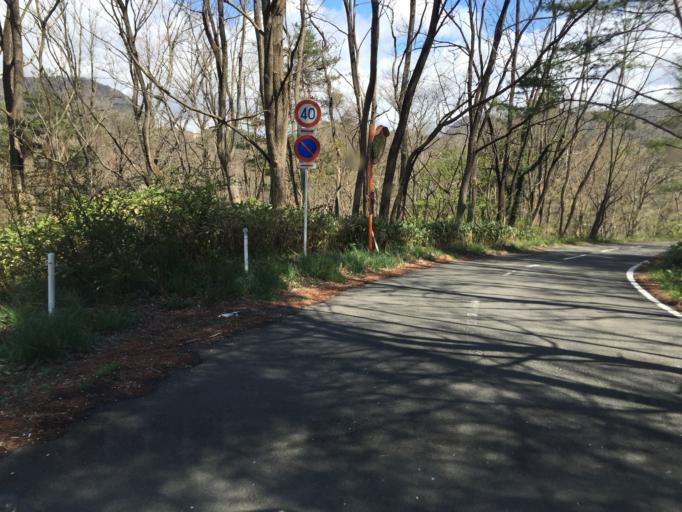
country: JP
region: Fukushima
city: Fukushima-shi
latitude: 37.8326
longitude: 140.4344
